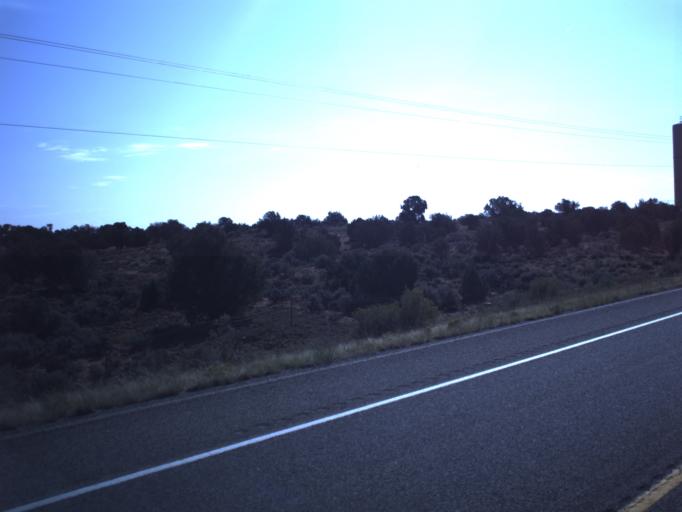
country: US
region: Utah
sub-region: San Juan County
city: Blanding
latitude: 37.4833
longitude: -109.4723
